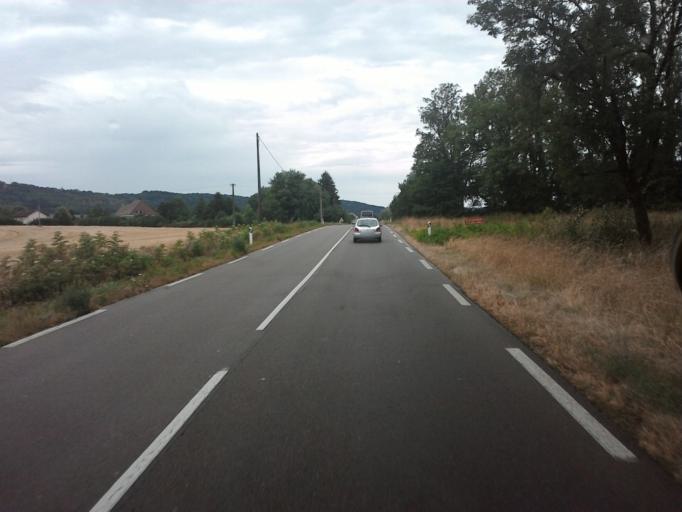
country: FR
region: Franche-Comte
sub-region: Departement du Jura
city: Poligny
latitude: 46.8740
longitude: 5.7162
